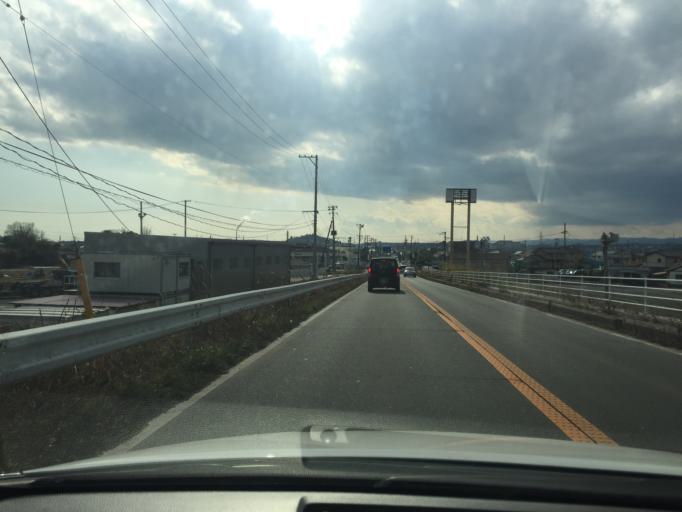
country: JP
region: Fukushima
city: Iwaki
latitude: 36.9568
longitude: 140.8687
